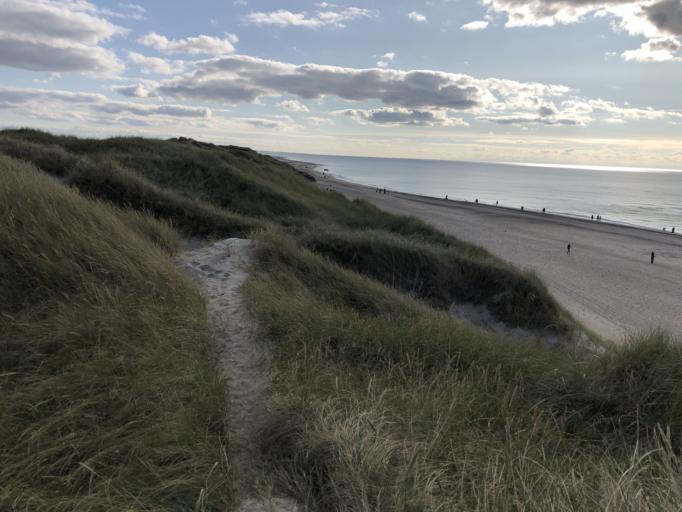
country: DK
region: Central Jutland
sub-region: Holstebro Kommune
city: Ulfborg
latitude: 56.3174
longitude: 8.1227
